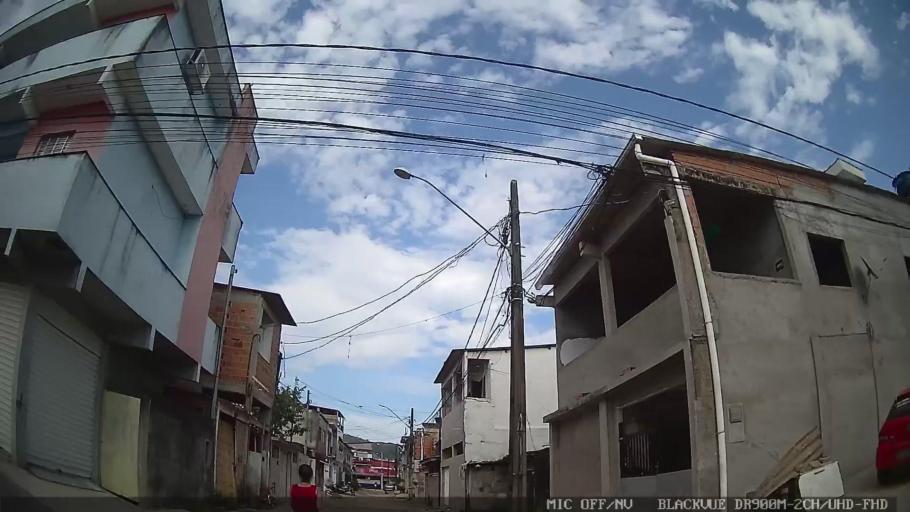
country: BR
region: Sao Paulo
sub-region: Guaruja
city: Guaruja
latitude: -23.9598
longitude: -46.2492
